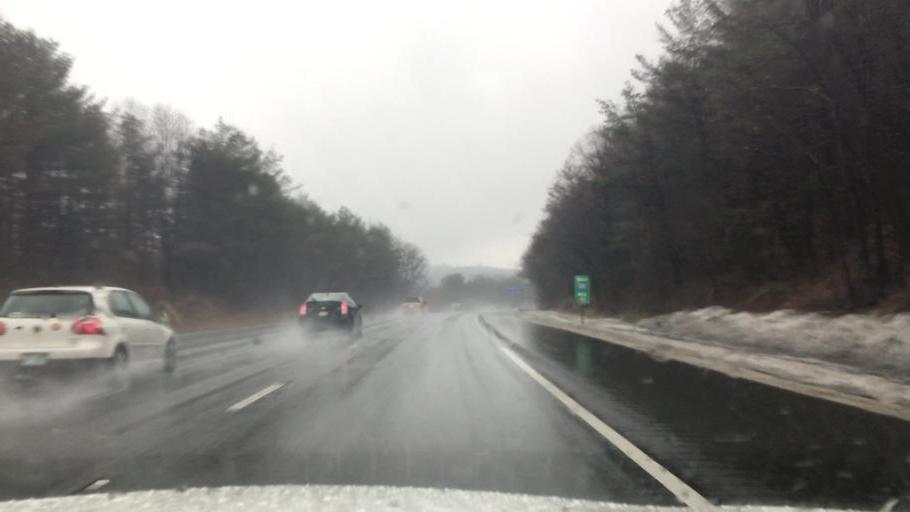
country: US
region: Massachusetts
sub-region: Essex County
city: Haverhill
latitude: 42.8058
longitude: -71.0763
